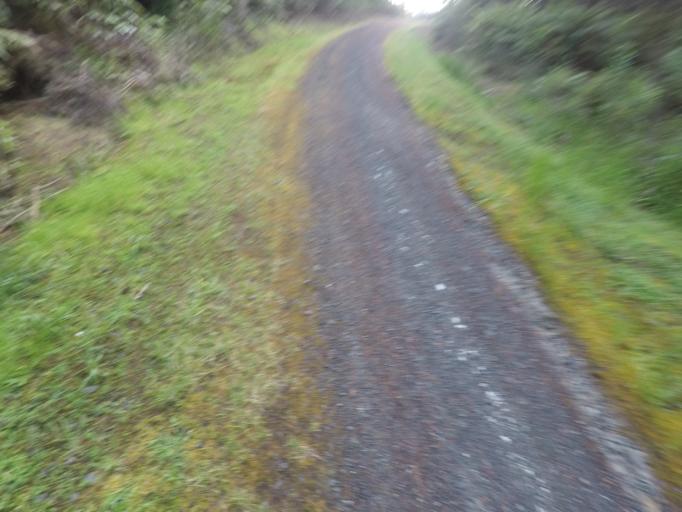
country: NZ
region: Auckland
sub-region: Auckland
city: Parakai
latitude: -36.7082
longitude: 174.5792
